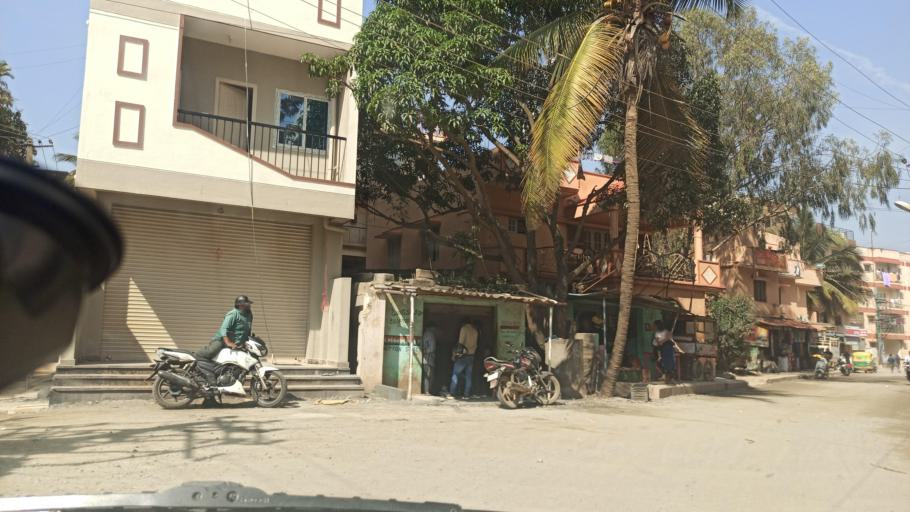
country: IN
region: Karnataka
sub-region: Bangalore Urban
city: Bangalore
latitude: 12.9265
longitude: 77.6897
